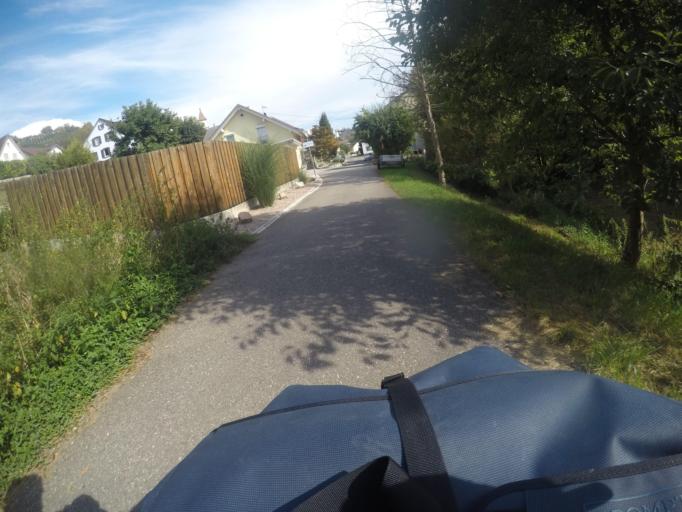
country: FR
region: Alsace
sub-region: Departement du Haut-Rhin
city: Rosenau
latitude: 47.6615
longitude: 7.5355
